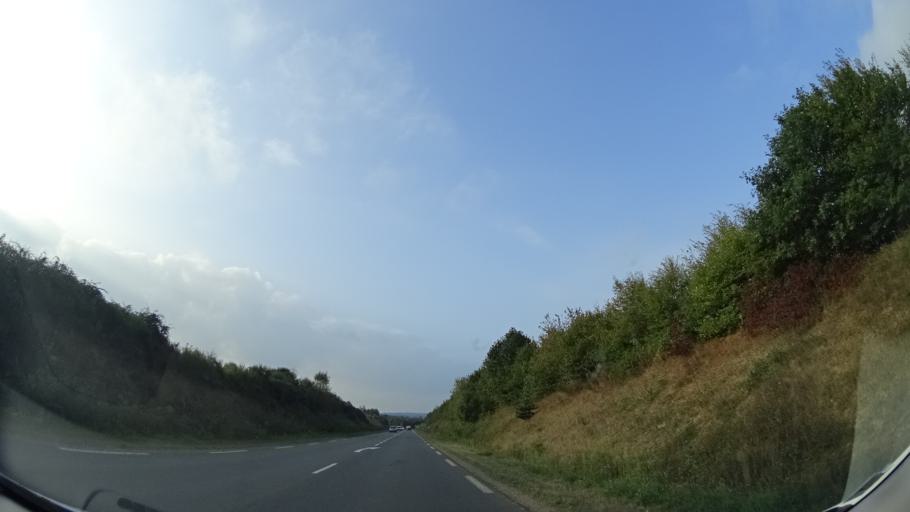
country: FR
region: Brittany
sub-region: Departement d'Ille-et-Vilaine
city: Montfort-sur-Meu
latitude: 48.1539
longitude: -1.9469
